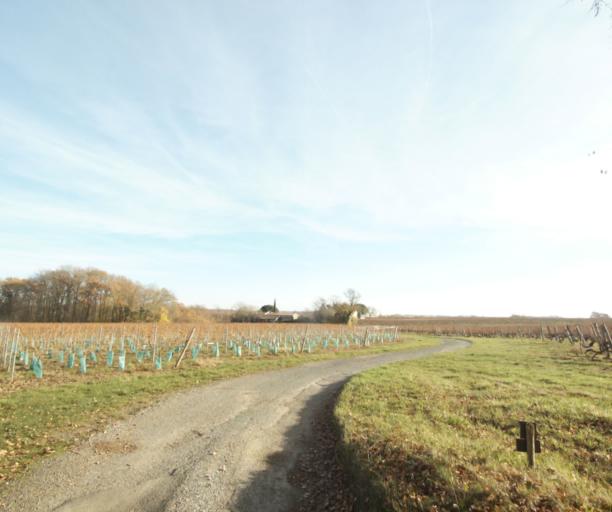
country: FR
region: Poitou-Charentes
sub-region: Departement de la Charente-Maritime
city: Chaniers
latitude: 45.7358
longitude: -0.5186
